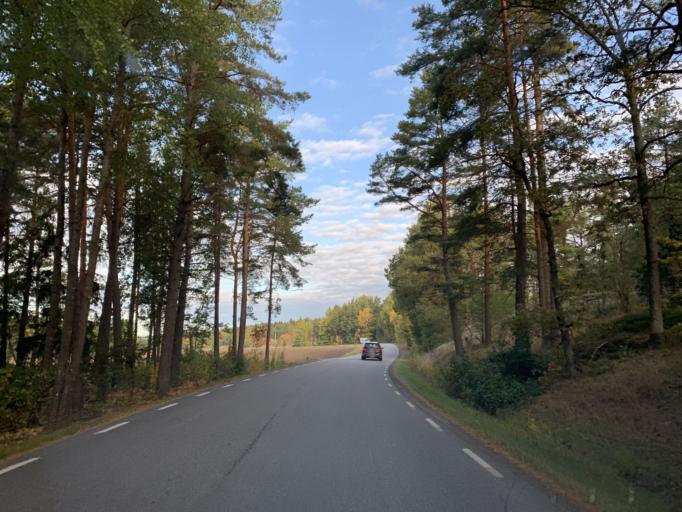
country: SE
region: Stockholm
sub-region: Upplands-Bro Kommun
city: Bro
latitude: 59.5062
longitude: 17.6053
